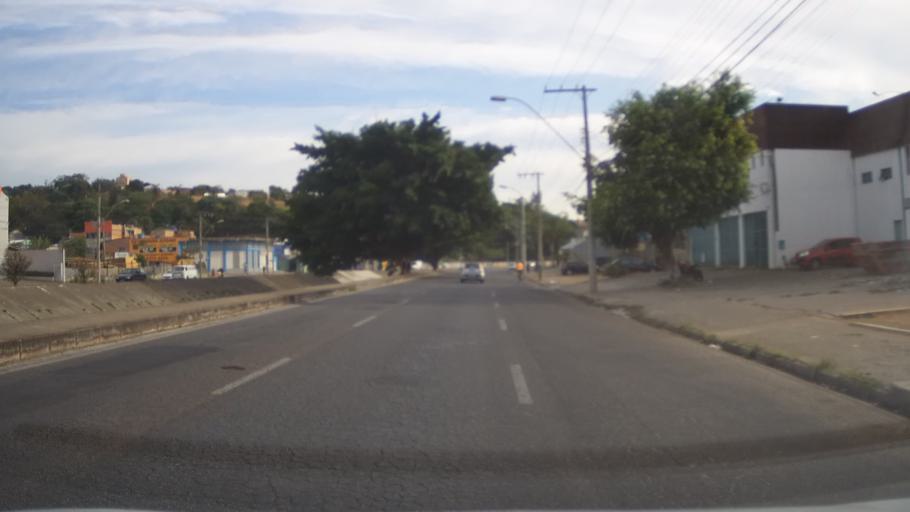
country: BR
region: Minas Gerais
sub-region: Contagem
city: Contagem
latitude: -19.8782
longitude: -44.0051
